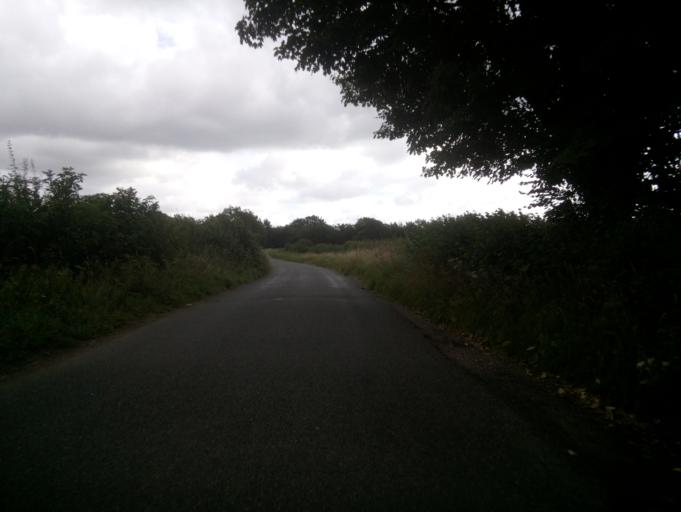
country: GB
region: England
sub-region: Gloucestershire
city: Chalford
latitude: 51.7857
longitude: -2.1115
